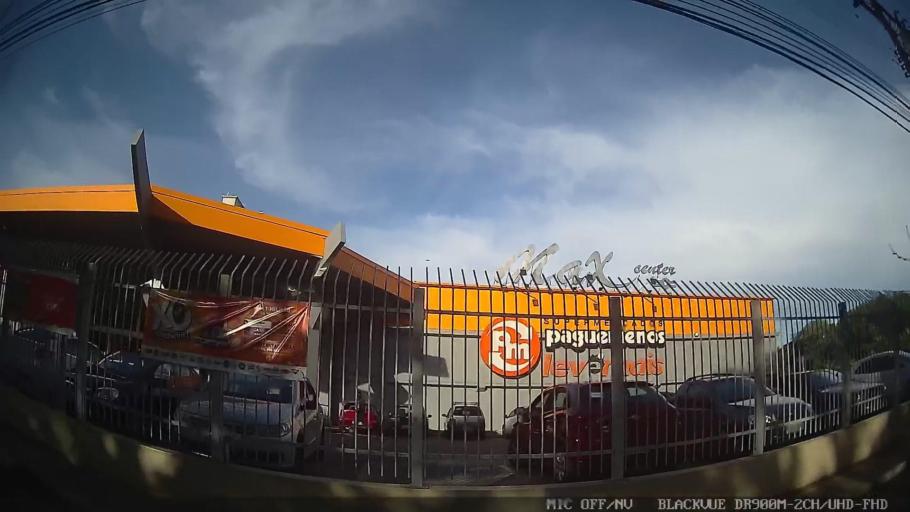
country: BR
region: Sao Paulo
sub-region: Tiete
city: Tiete
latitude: -23.0953
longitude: -47.7176
